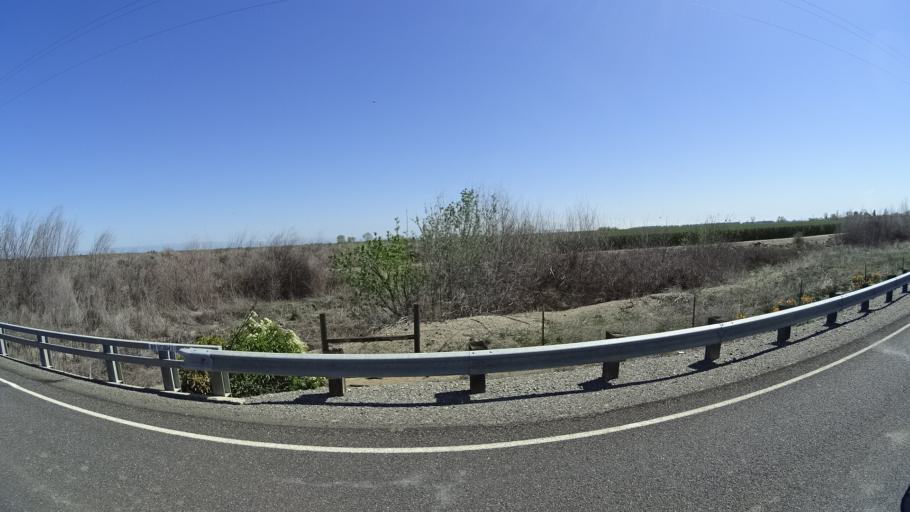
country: US
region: California
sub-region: Glenn County
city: Willows
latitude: 39.6174
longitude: -122.2500
